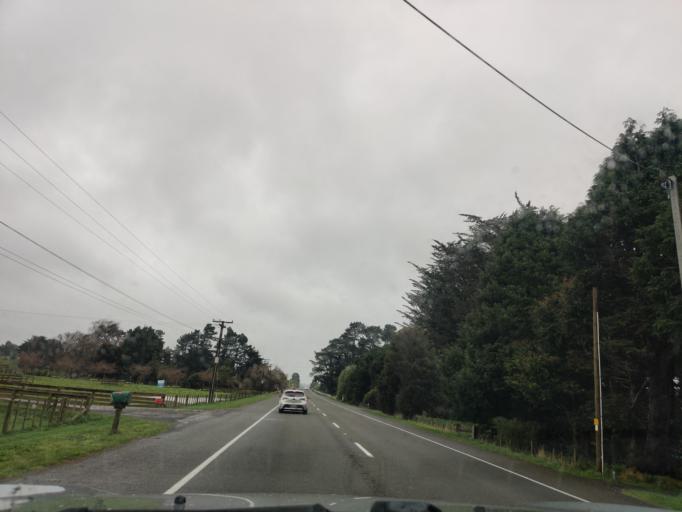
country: NZ
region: Manawatu-Wanganui
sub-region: Palmerston North City
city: Palmerston North
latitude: -40.0648
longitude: 176.2240
